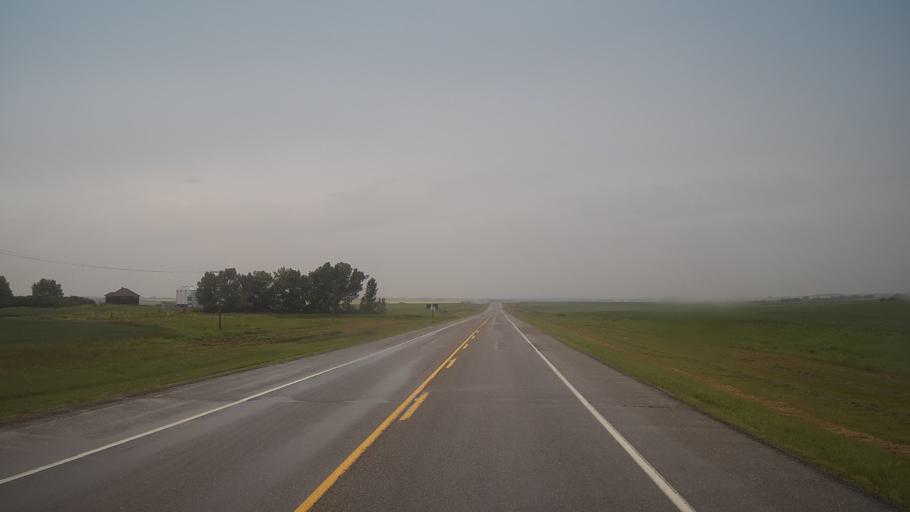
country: CA
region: Saskatchewan
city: Wilkie
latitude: 52.2041
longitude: -108.4754
